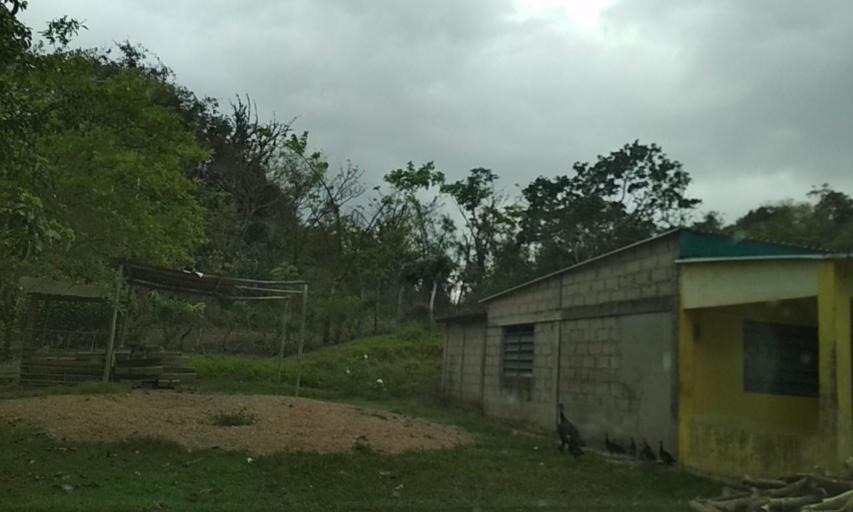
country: MX
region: Tabasco
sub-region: Huimanguillo
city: Francisco Rueda
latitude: 17.6539
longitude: -94.0967
